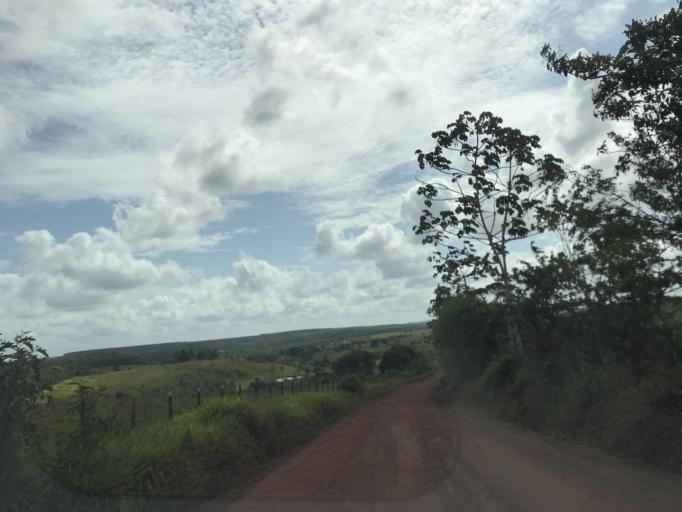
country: BR
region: Bahia
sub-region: Entre Rios
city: Entre Rios
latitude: -12.1701
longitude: -38.1018
